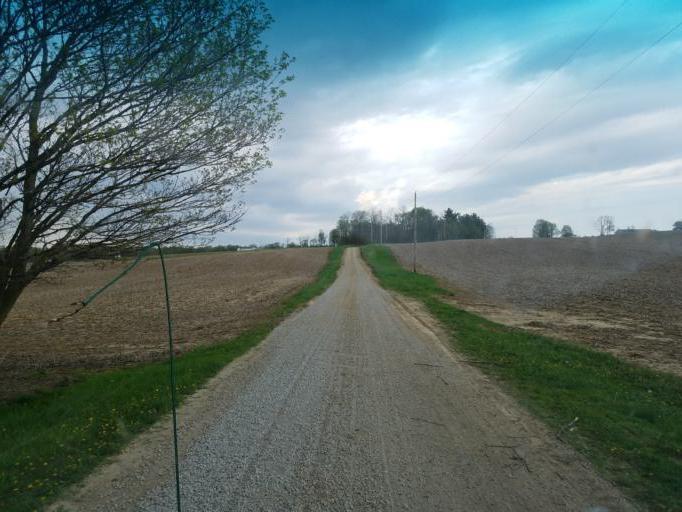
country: US
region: Ohio
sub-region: Morrow County
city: Mount Gilead
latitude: 40.5612
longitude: -82.6861
